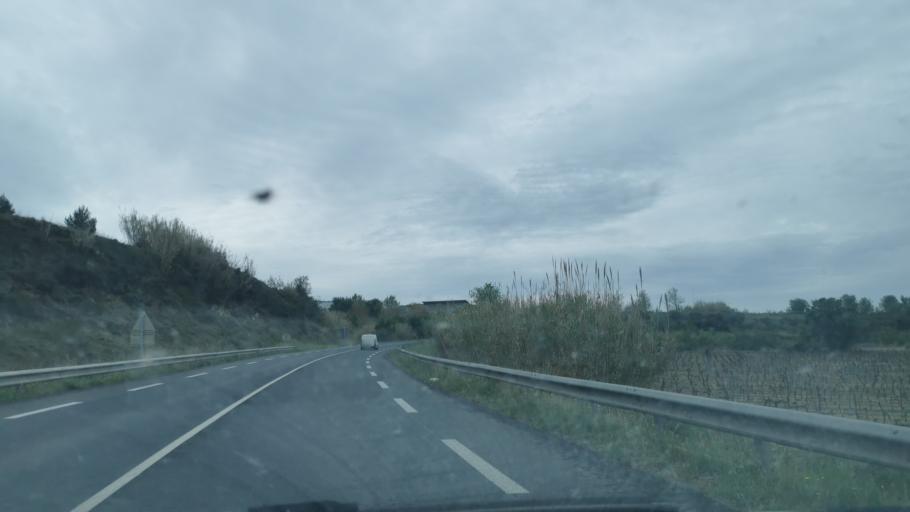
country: FR
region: Languedoc-Roussillon
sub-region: Departement de l'Herault
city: Gigean
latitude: 43.4939
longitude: 3.7001
